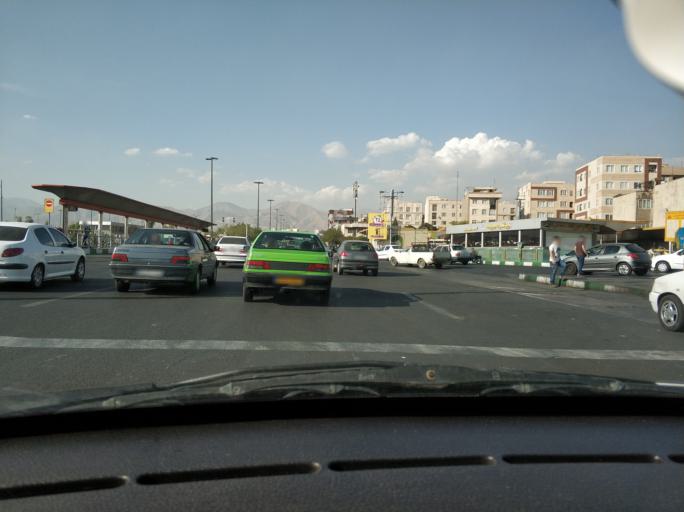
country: IR
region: Tehran
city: Tehran
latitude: 35.7020
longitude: 51.3379
